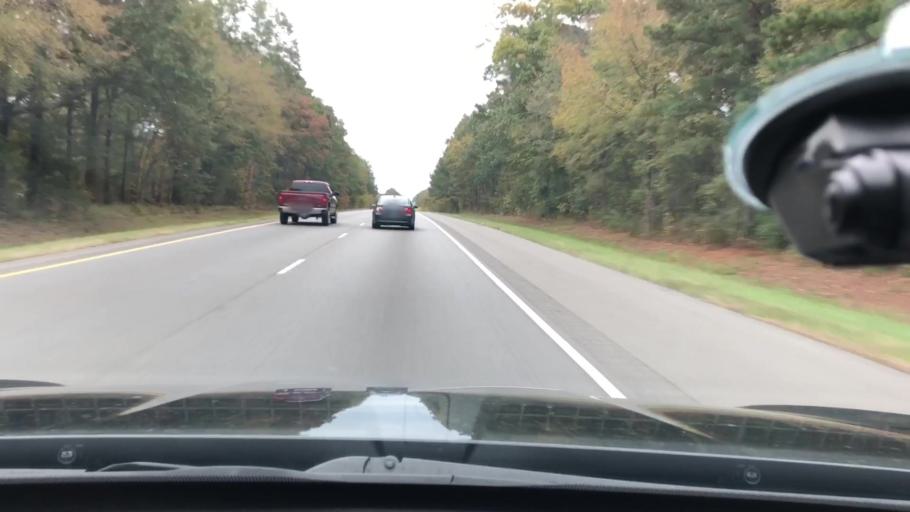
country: US
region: Arkansas
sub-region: Hempstead County
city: Hope
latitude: 33.6373
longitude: -93.7058
